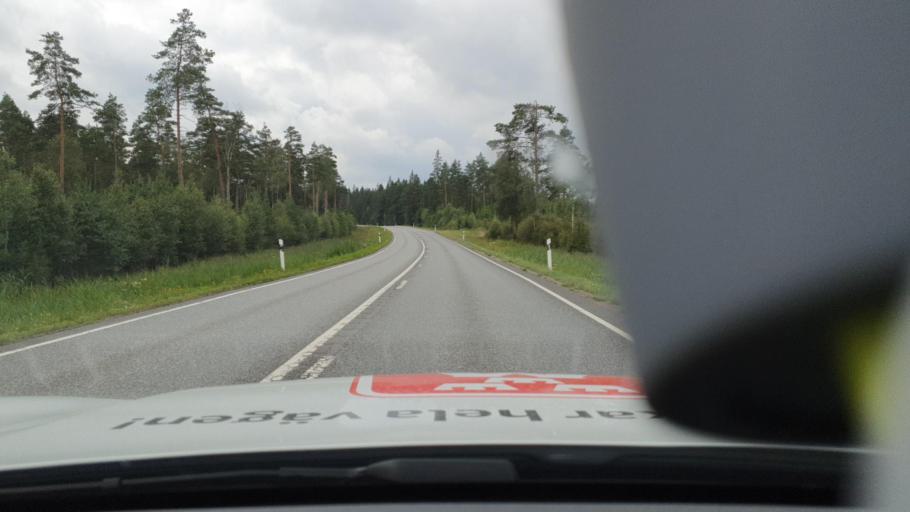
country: SE
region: Joenkoeping
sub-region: Gislaveds Kommun
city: Smalandsstenar
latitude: 57.2341
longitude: 13.4409
